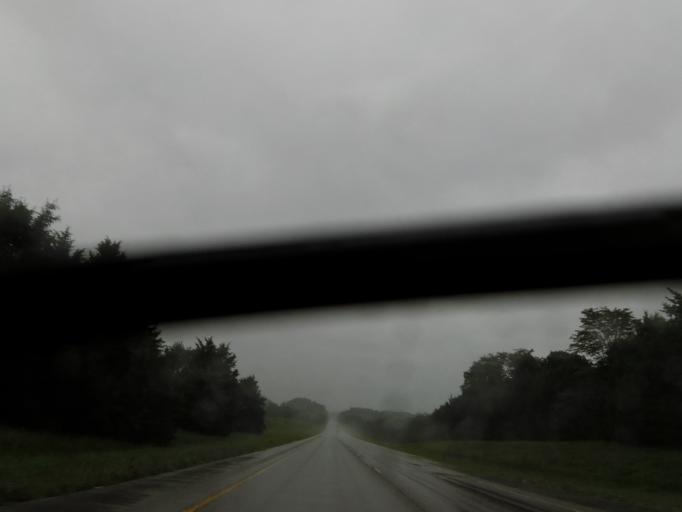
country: US
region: Illinois
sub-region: Johnson County
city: Vienna
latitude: 37.4703
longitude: -88.8911
